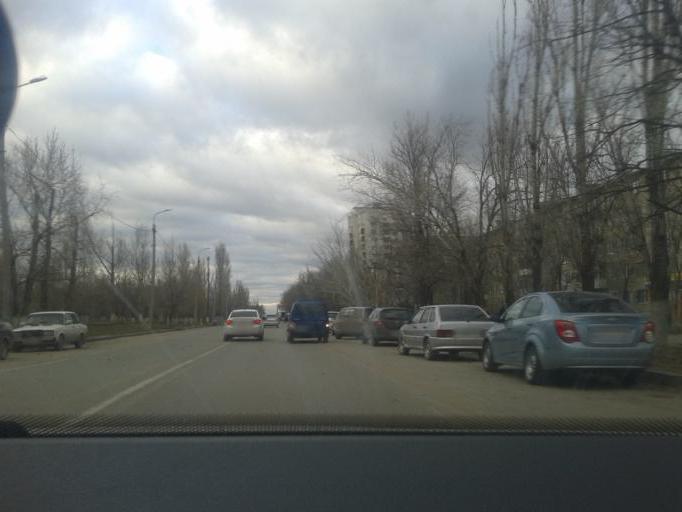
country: RU
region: Volgograd
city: Gorodishche
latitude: 48.7629
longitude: 44.4785
